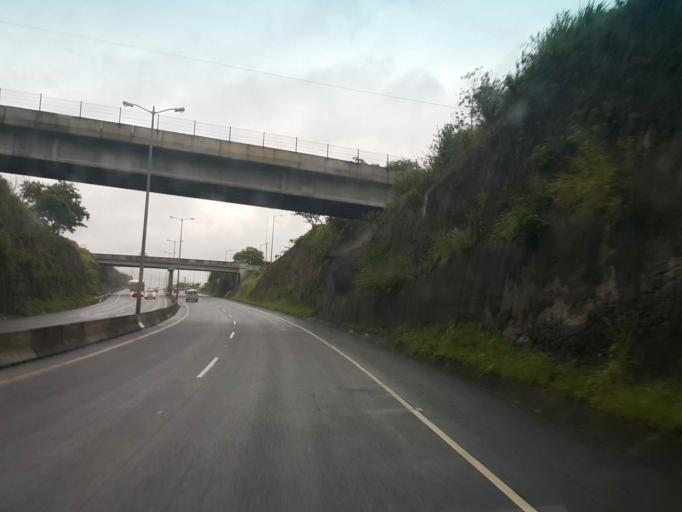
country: CR
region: Heredia
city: Colon
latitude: 9.9369
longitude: -84.2211
